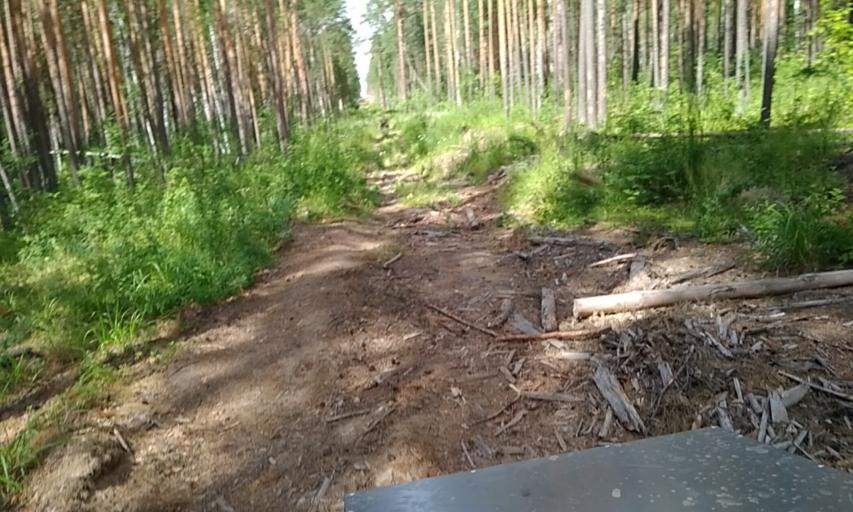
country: RU
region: Tomsk
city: Timiryazevskoye
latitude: 56.4064
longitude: 84.6640
